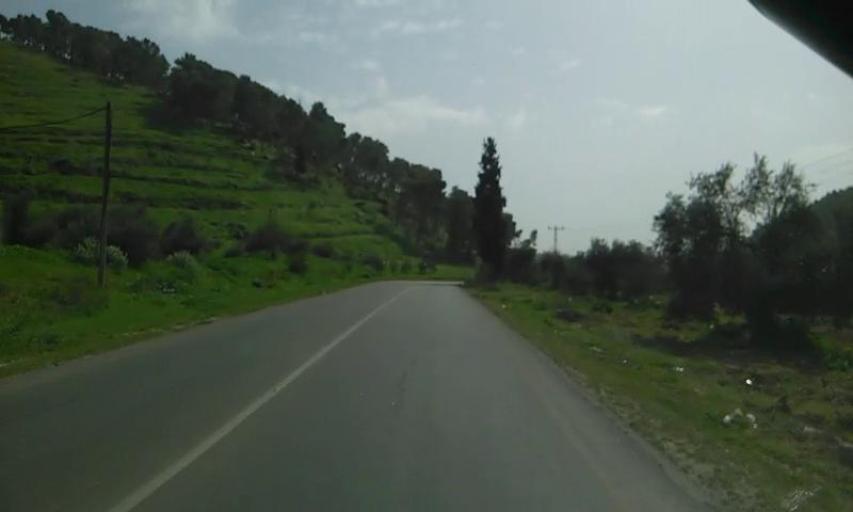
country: PS
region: West Bank
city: Mirkah
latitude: 32.4015
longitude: 35.2251
